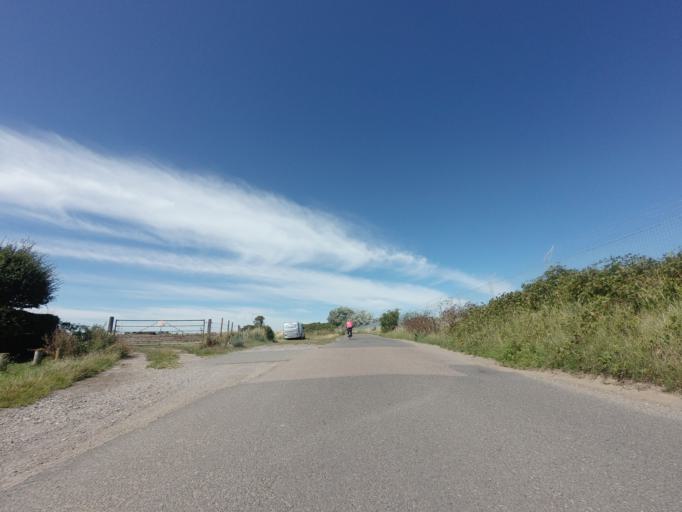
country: GB
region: England
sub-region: Kent
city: Deal
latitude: 51.2513
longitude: 1.3916
